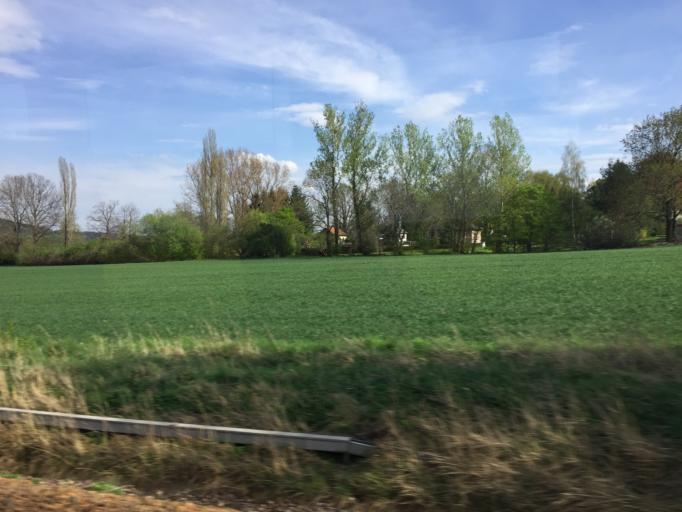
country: DE
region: Saxony
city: Lobau
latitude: 51.1097
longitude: 14.7077
